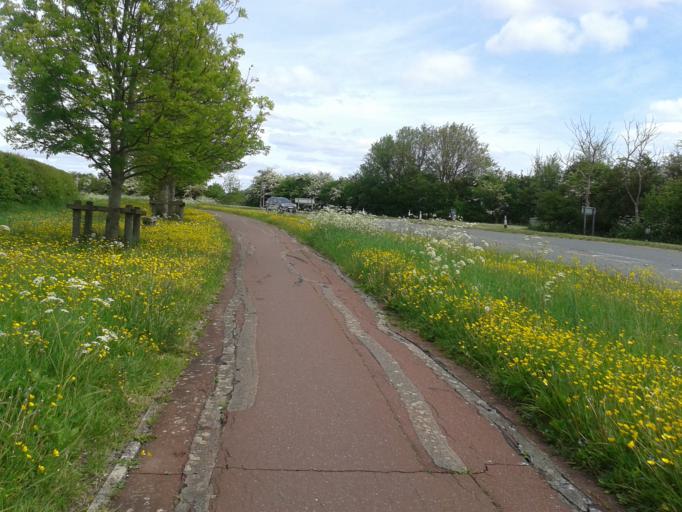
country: GB
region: England
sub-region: Cambridgeshire
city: Barton
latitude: 52.1786
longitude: 0.0641
